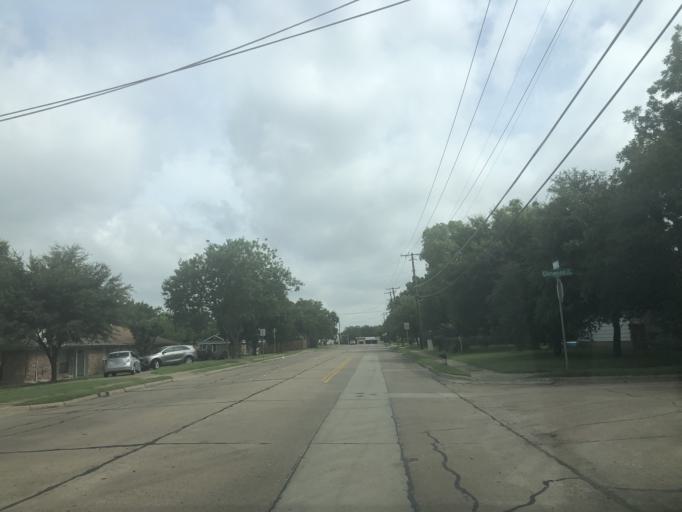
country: US
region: Texas
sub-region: Dallas County
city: Irving
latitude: 32.8059
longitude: -96.9631
